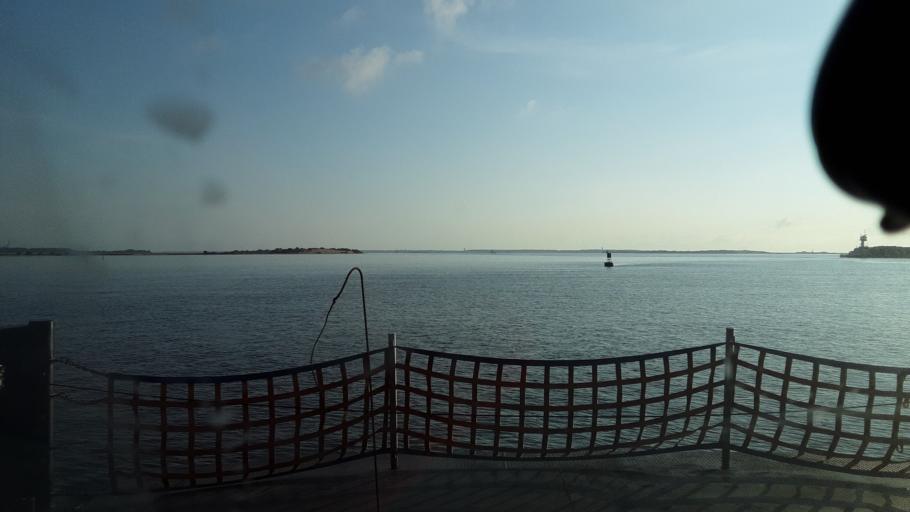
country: US
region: North Carolina
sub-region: Brunswick County
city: Southport
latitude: 33.9453
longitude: -77.9713
